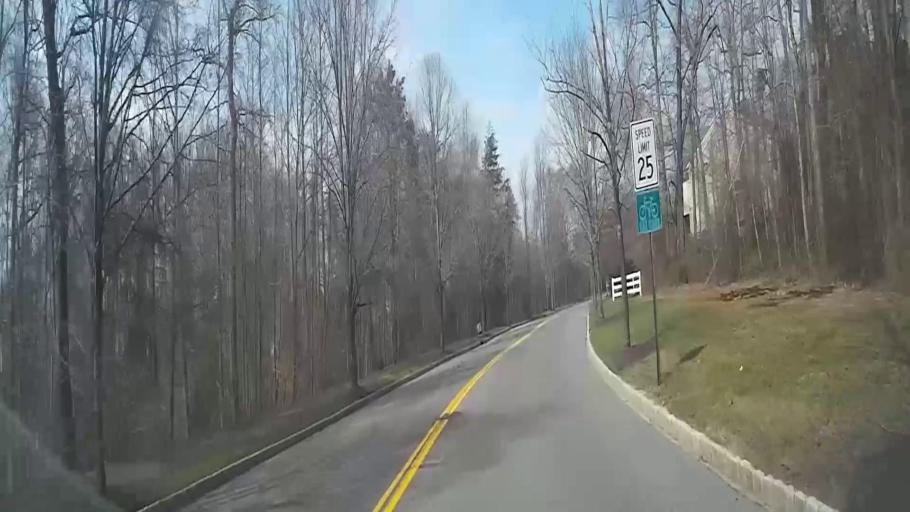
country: US
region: New Jersey
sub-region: Burlington County
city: Marlton
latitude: 39.8682
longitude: -74.8664
